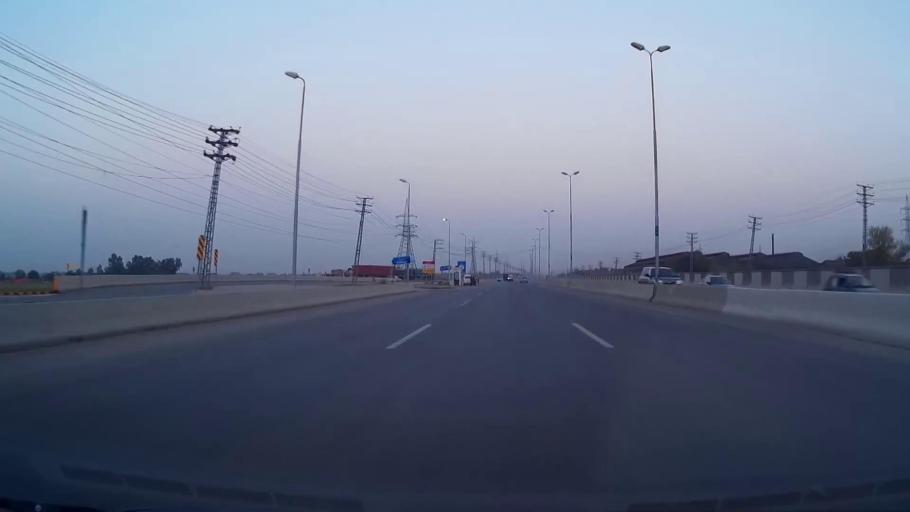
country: PK
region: Punjab
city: Lahore
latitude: 31.6096
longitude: 74.3237
